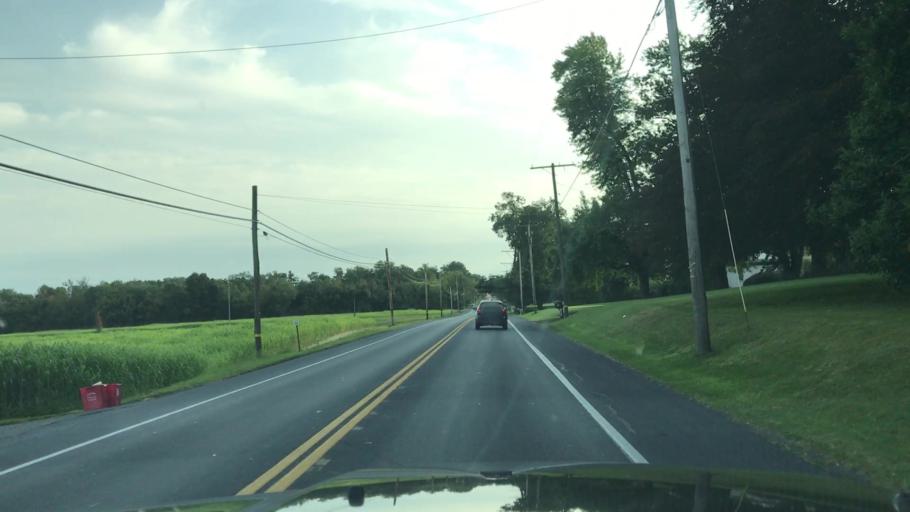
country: US
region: Pennsylvania
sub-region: Berks County
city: Bally
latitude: 40.4112
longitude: -75.5791
